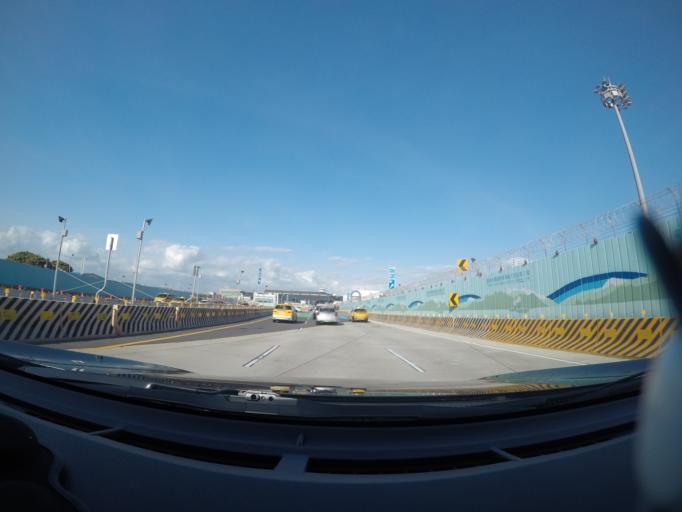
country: TW
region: Taiwan
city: Taoyuan City
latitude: 25.0710
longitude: 121.2275
